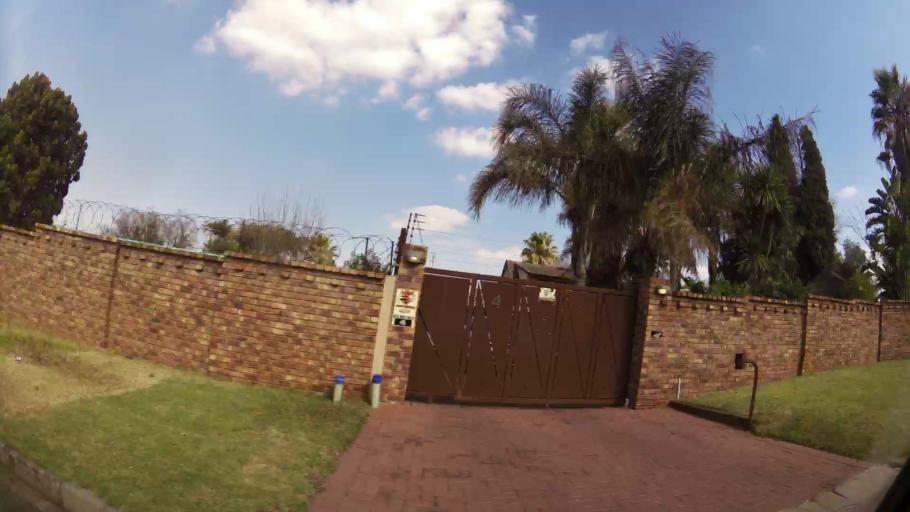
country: ZA
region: Gauteng
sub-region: Ekurhuleni Metropolitan Municipality
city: Germiston
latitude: -26.1782
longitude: 28.1974
